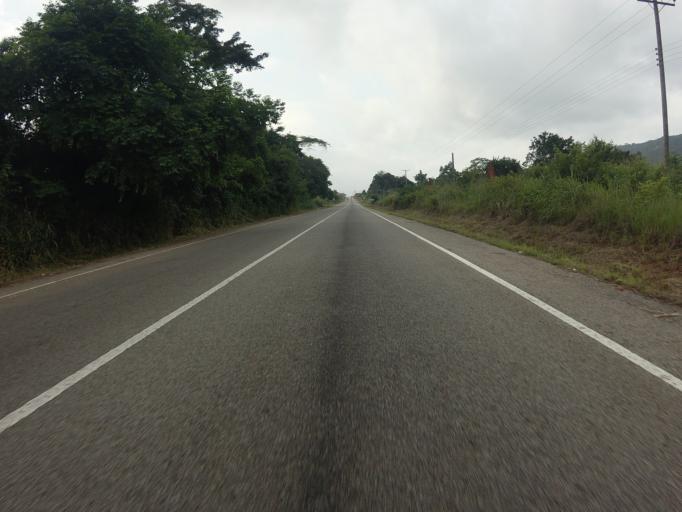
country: GH
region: Volta
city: Ho
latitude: 6.6540
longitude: 0.4700
